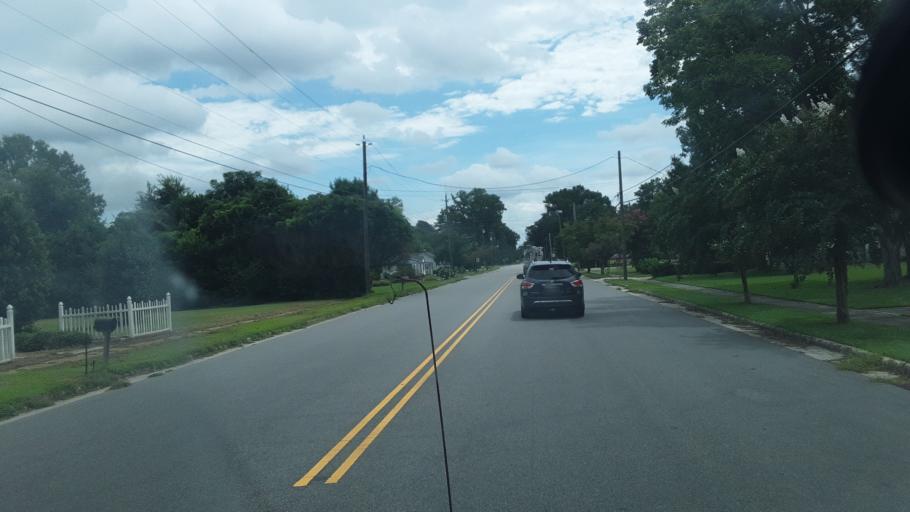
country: US
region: North Carolina
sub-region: Robeson County
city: Rowland
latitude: 34.5352
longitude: -79.2882
